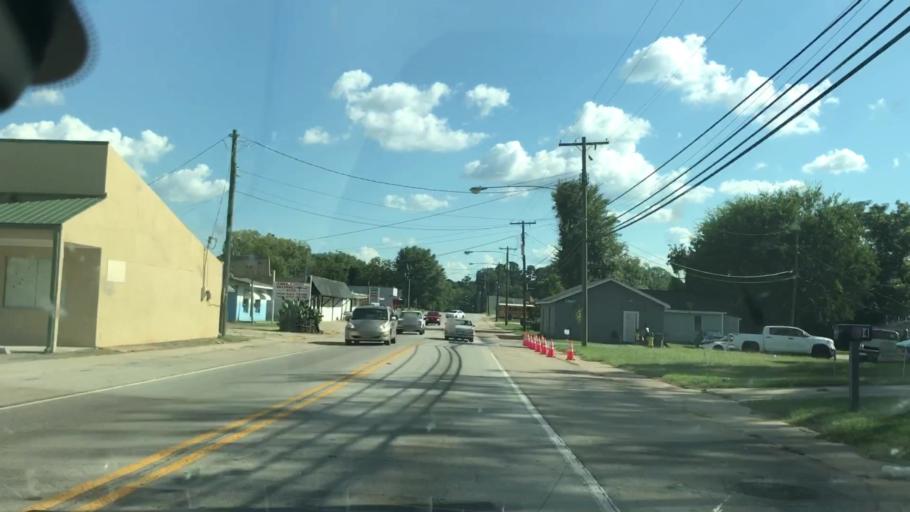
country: US
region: Georgia
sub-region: Troup County
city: La Grange
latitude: 33.0271
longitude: -85.0238
